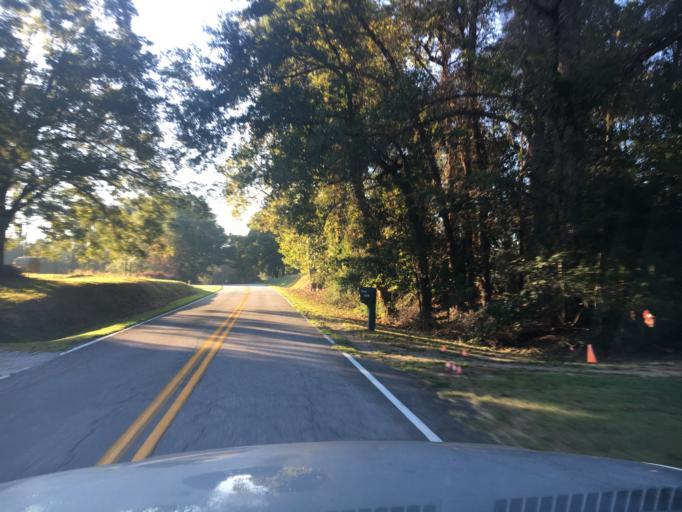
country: US
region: South Carolina
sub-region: Spartanburg County
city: Woodruff
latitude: 34.7889
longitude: -82.0047
